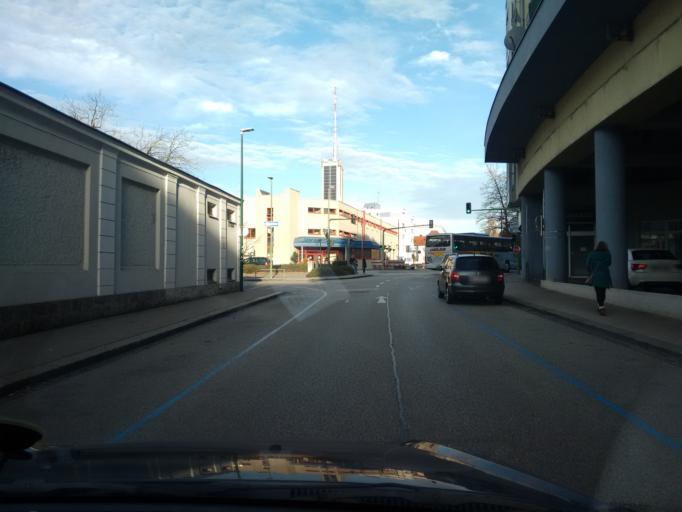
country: AT
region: Upper Austria
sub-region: Wels-Land
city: Thalheim bei Wels
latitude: 48.1578
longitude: 14.0194
